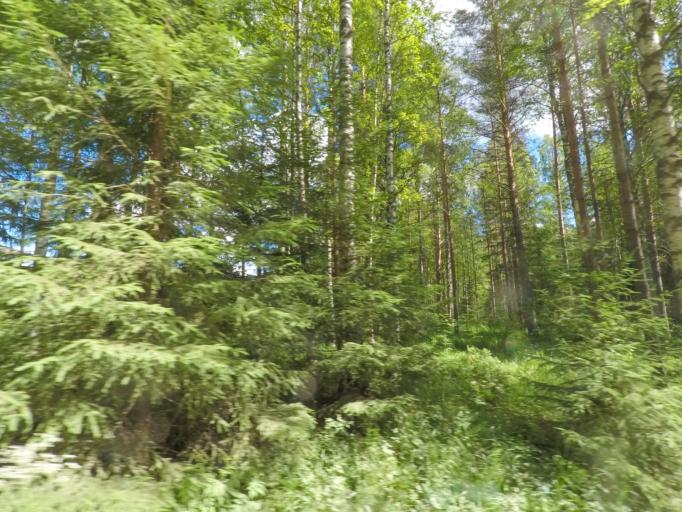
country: FI
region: Central Finland
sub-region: Jyvaeskylae
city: Hankasalmi
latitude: 62.4364
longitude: 26.6471
